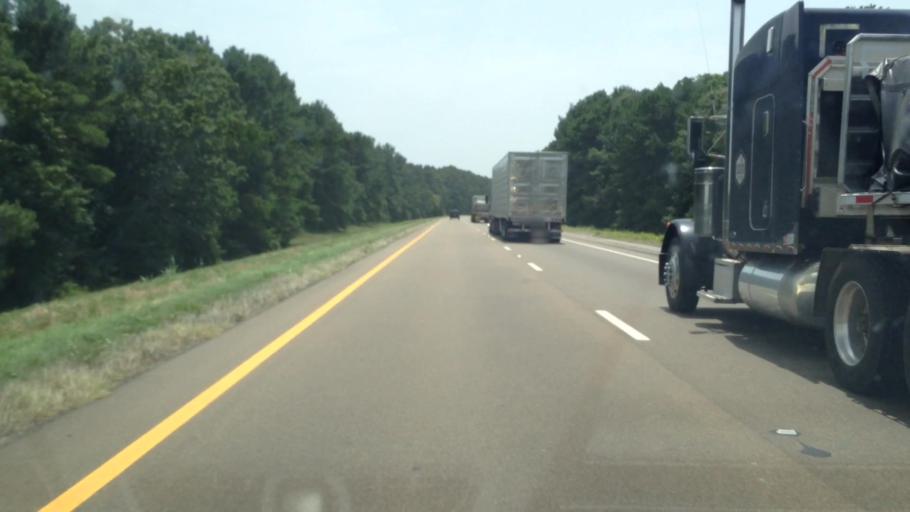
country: US
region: Texas
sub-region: Morris County
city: Naples
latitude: 33.3031
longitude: -94.7076
